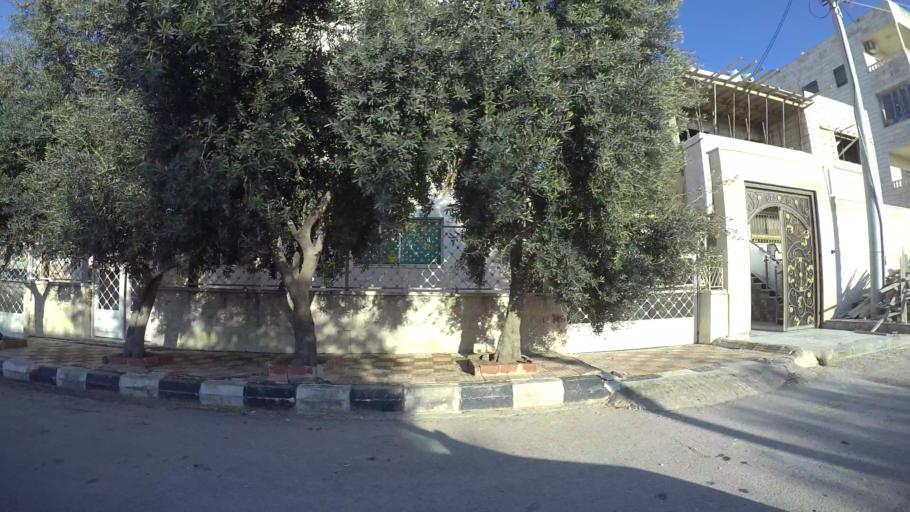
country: JO
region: Amman
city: Al Bunayyat ash Shamaliyah
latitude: 31.8996
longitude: 35.9080
